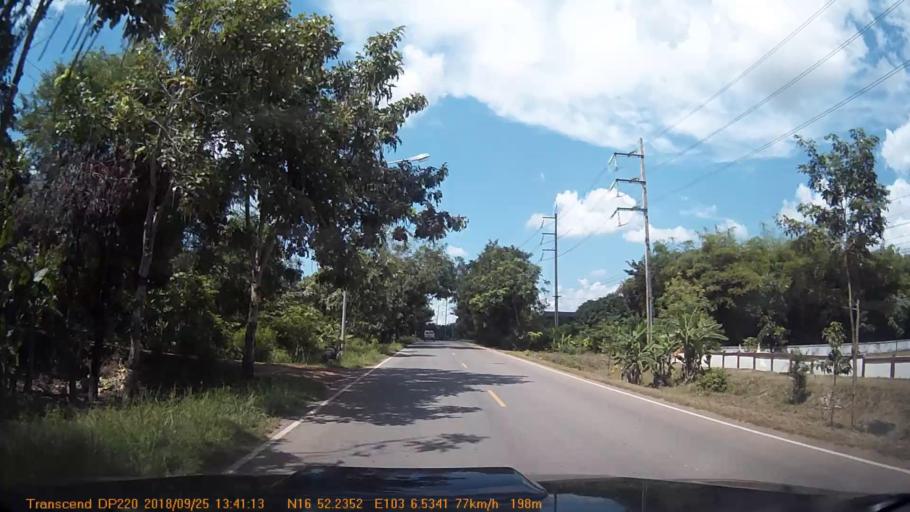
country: TH
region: Changwat Udon Thani
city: Si That
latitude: 16.8707
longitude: 103.1089
